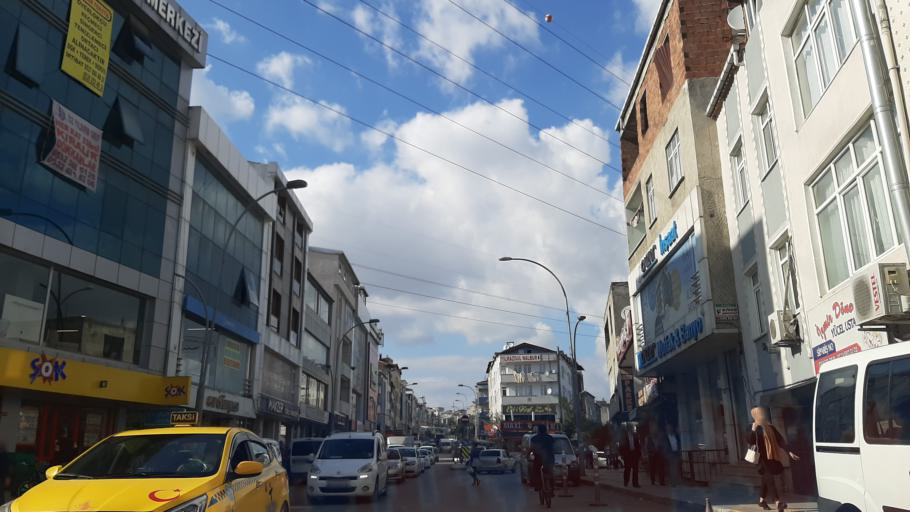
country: TR
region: Istanbul
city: Esenyurt
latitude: 41.0324
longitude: 28.6611
